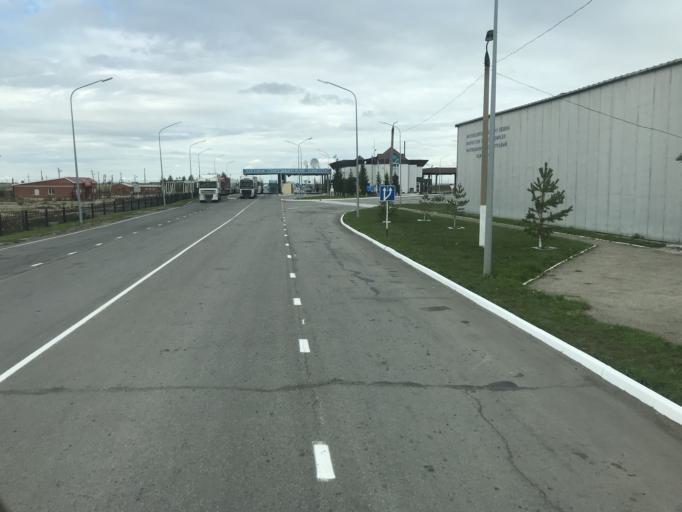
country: RU
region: Chelyabinsk
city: Bobrovka
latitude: 53.9995
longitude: 61.6403
